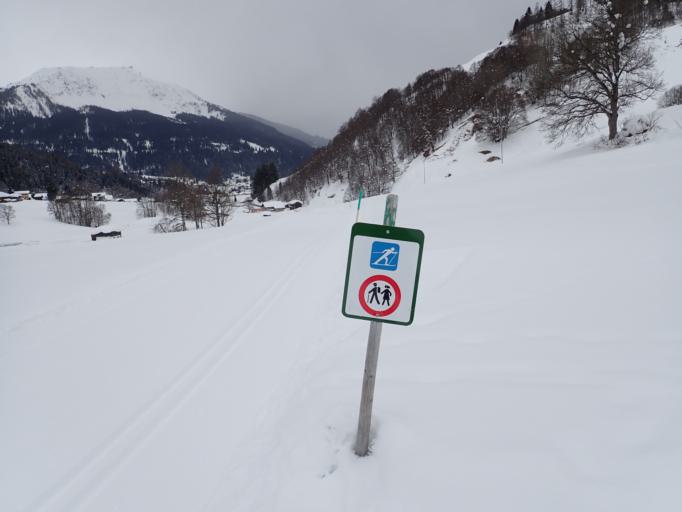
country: CH
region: Grisons
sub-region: Praettigau/Davos District
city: Klosters Serneus
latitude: 46.8621
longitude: 9.9141
